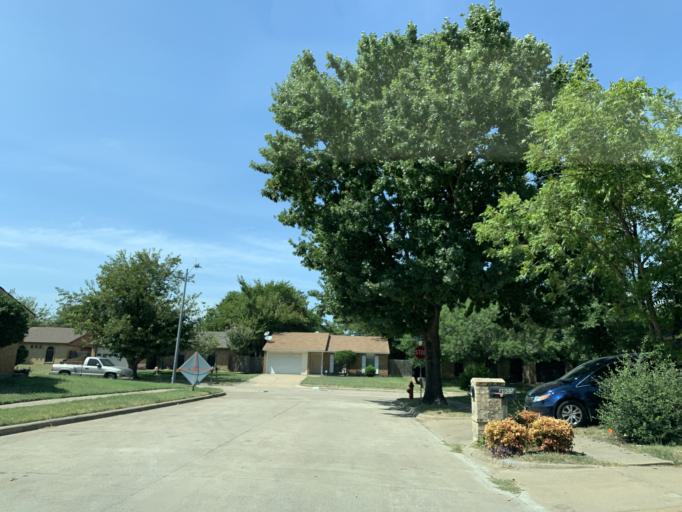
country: US
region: Texas
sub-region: Dallas County
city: Cedar Hill
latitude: 32.6518
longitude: -97.0176
